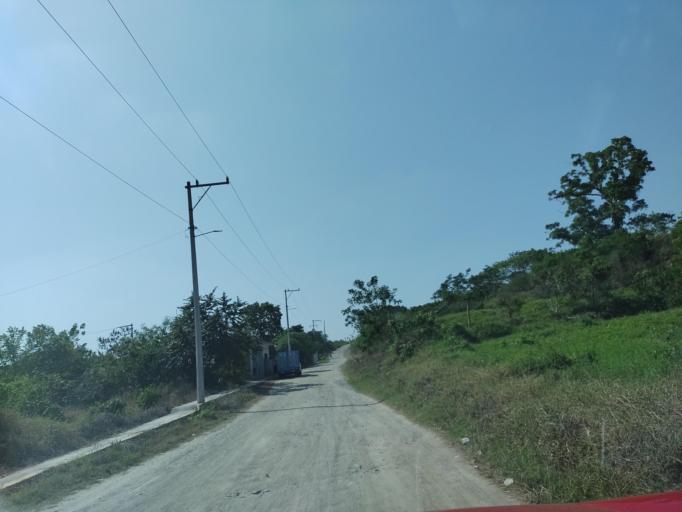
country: MX
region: Puebla
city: San Jose Acateno
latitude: 20.2564
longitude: -97.2087
